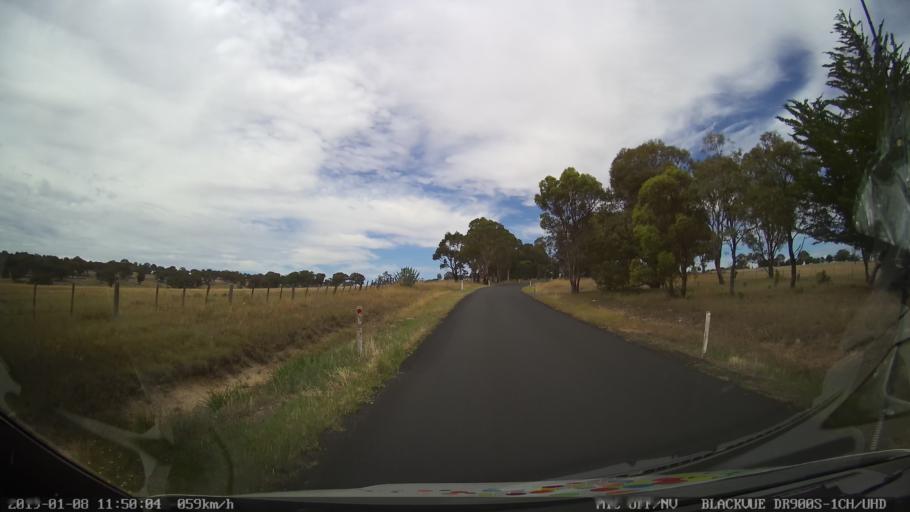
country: AU
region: New South Wales
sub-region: Armidale Dumaresq
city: Armidale
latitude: -30.3794
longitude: 151.5584
